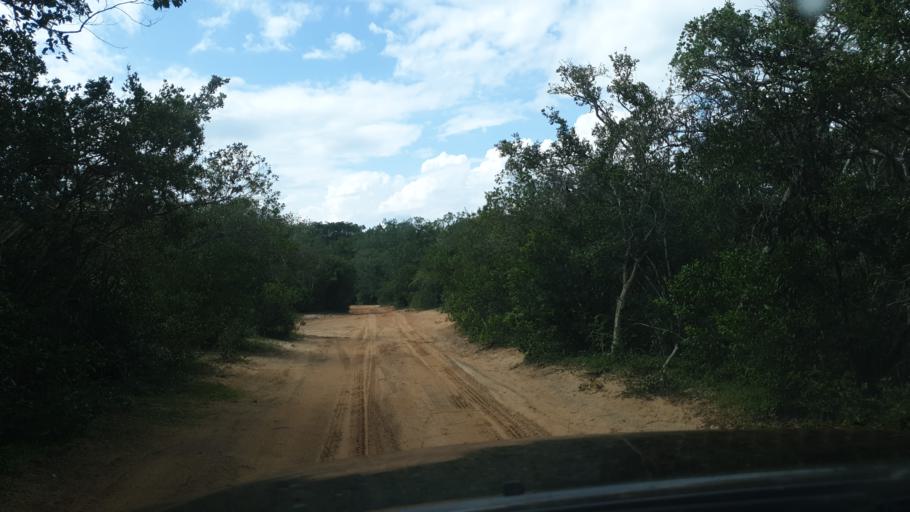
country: LK
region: North Central
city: Anuradhapura
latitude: 8.4194
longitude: 80.0157
